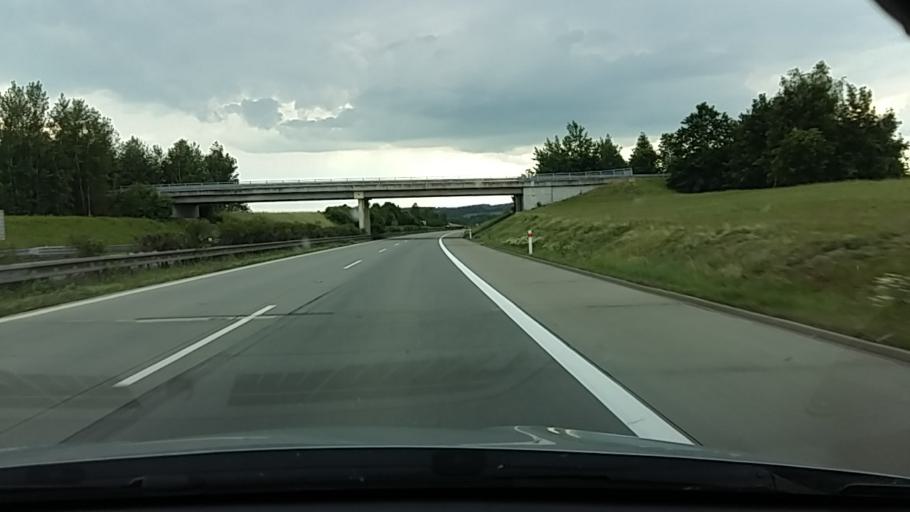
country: CZ
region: Plzensky
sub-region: Okres Tachov
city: Kladruby
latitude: 49.7025
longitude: 12.9881
